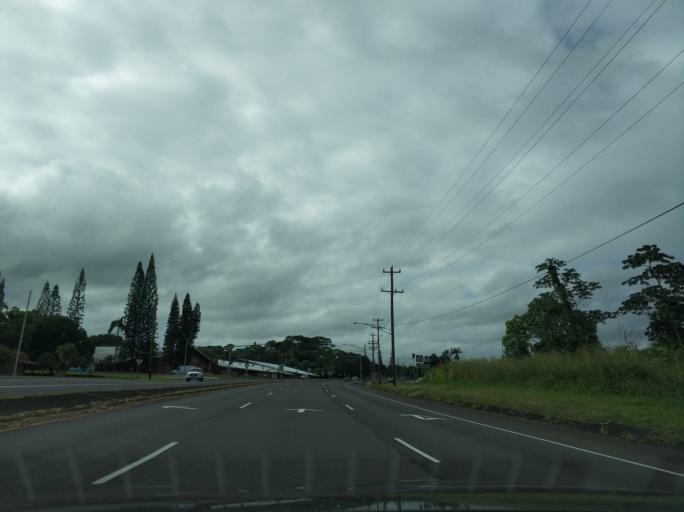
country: US
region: Hawaii
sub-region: Hawaii County
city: Kea'au
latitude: 19.6243
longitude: -155.0402
